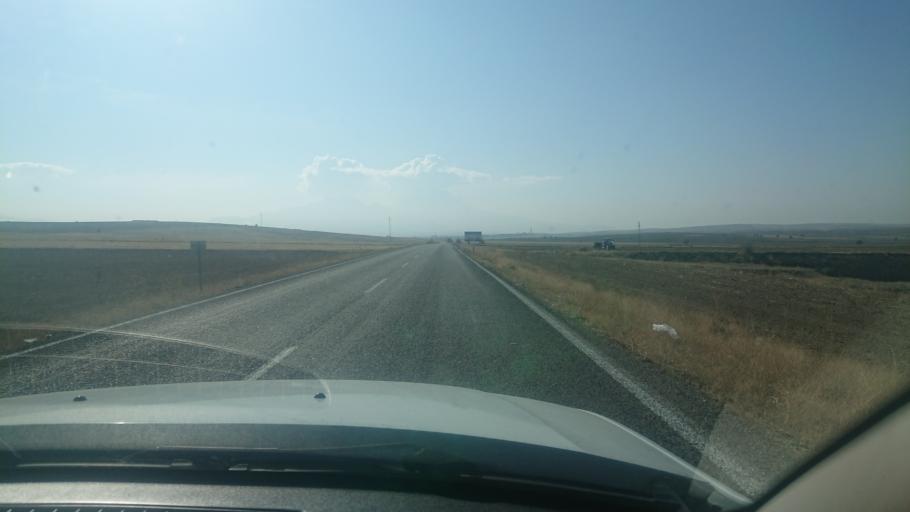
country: TR
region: Aksaray
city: Guzelyurt
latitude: 38.3044
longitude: 34.3220
